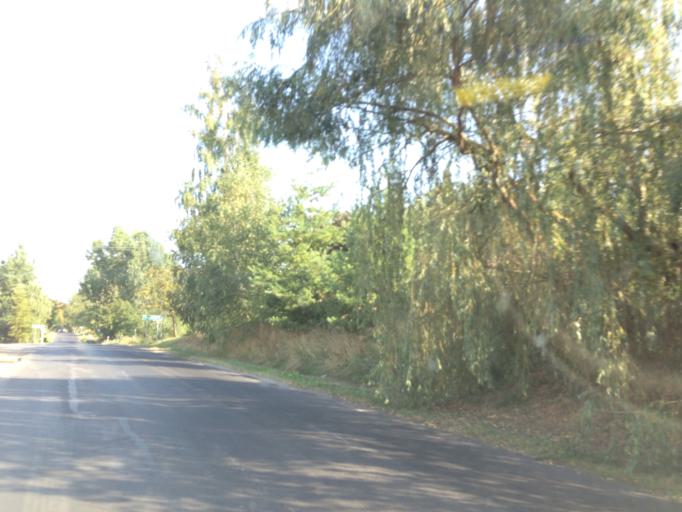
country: PL
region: Kujawsko-Pomorskie
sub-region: Powiat grudziadzki
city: Lasin
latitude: 53.5176
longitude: 19.1491
